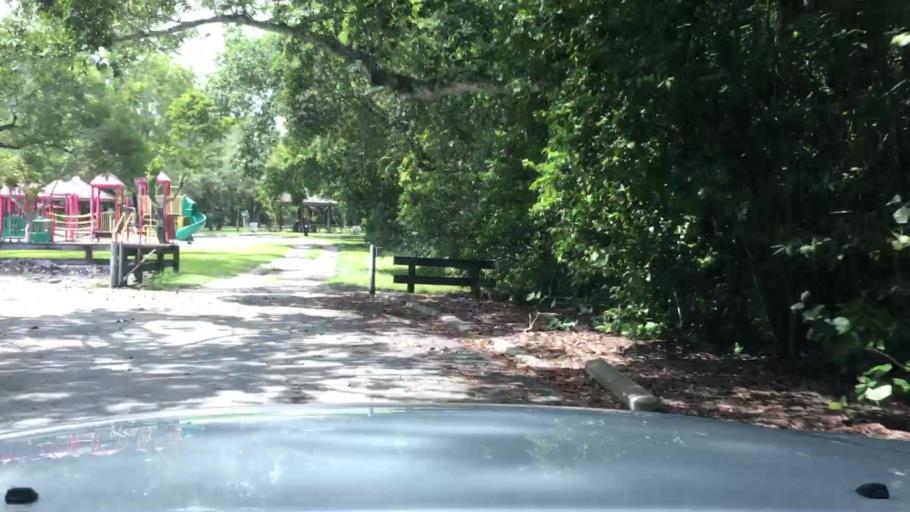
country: US
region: Florida
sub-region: Miami-Dade County
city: Ojus
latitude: 25.9424
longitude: -80.1532
